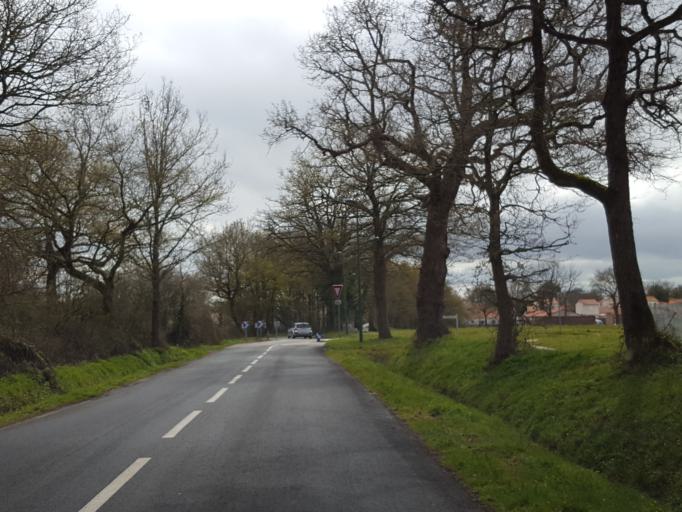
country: FR
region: Pays de la Loire
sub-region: Departement de la Vendee
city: La Roche-sur-Yon
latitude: 46.6714
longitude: -1.3978
